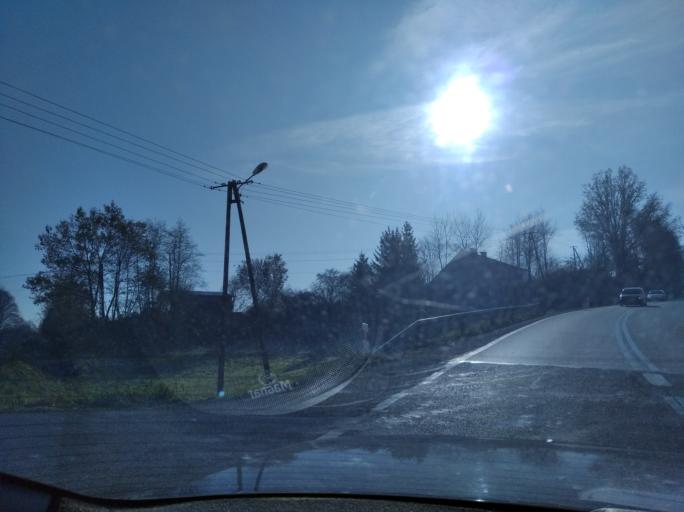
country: PL
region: Subcarpathian Voivodeship
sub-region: Powiat ropczycko-sedziszowski
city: Wielopole Skrzynskie
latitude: 49.9393
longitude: 21.6167
